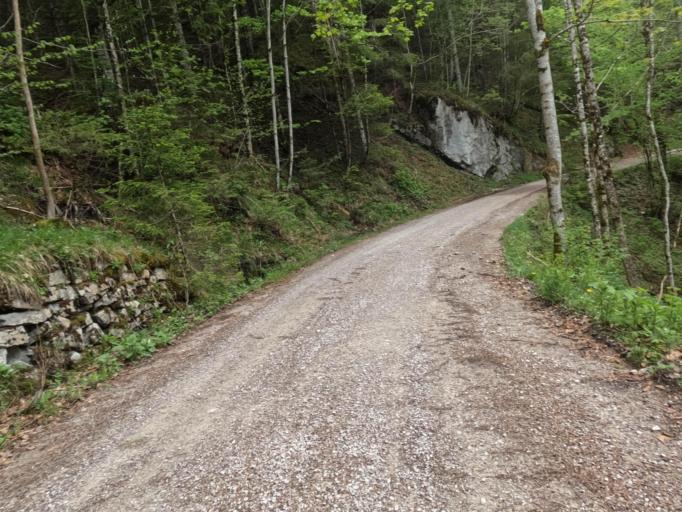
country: DE
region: Bavaria
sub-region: Upper Bavaria
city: Ruhpolding
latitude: 47.7105
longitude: 12.6753
